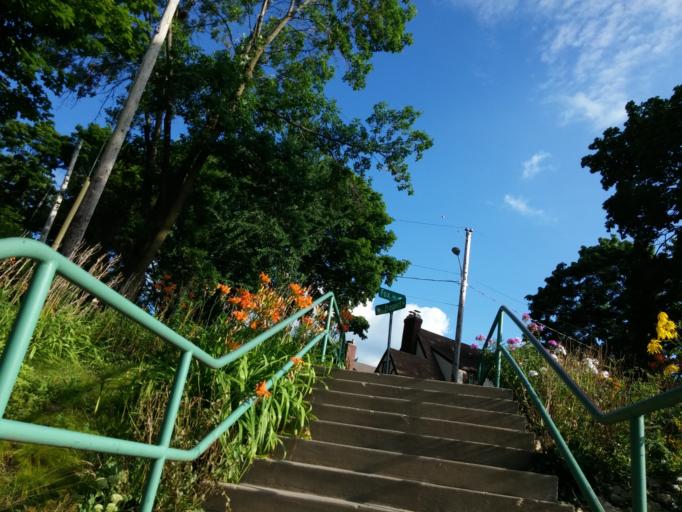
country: US
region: Wisconsin
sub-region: Dane County
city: Madison
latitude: 43.0657
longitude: -89.4213
